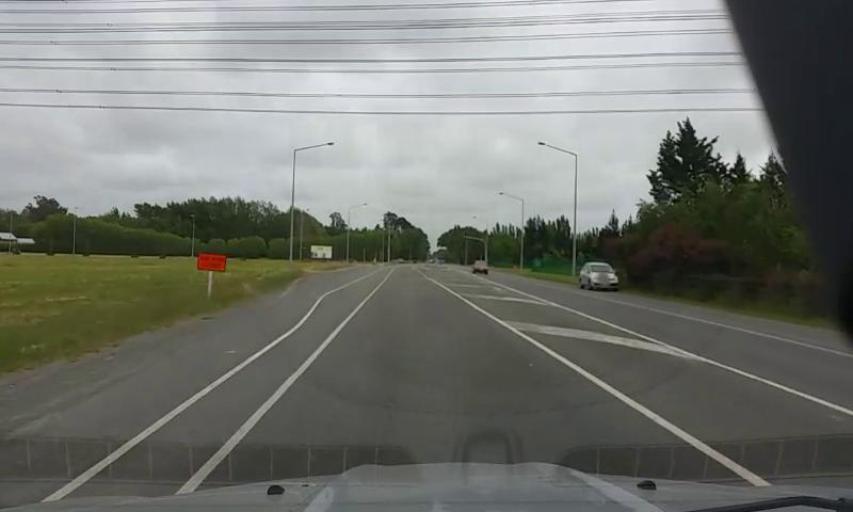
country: NZ
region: Canterbury
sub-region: Selwyn District
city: Prebbleton
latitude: -43.5186
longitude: 172.5286
